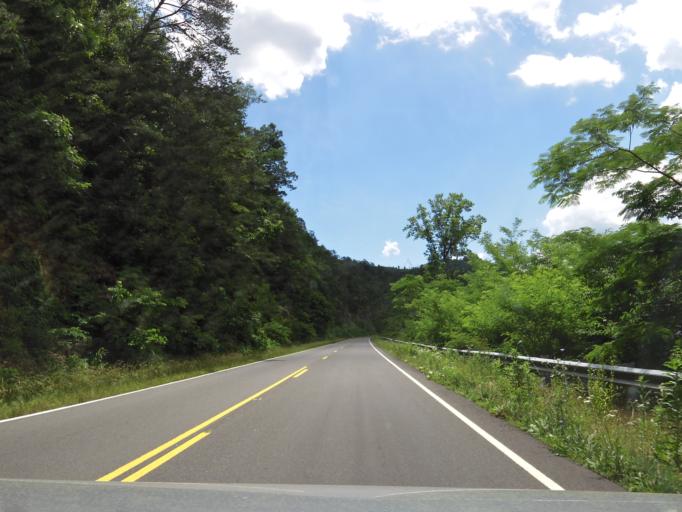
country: US
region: Tennessee
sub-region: Blount County
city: Maryville
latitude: 35.5534
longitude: -83.9949
